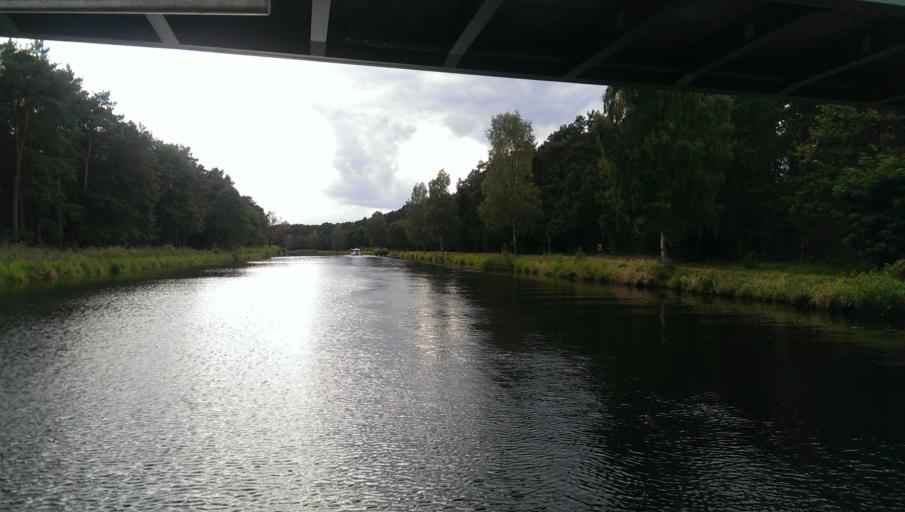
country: DE
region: Brandenburg
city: Oranienburg
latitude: 52.7923
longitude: 13.2880
